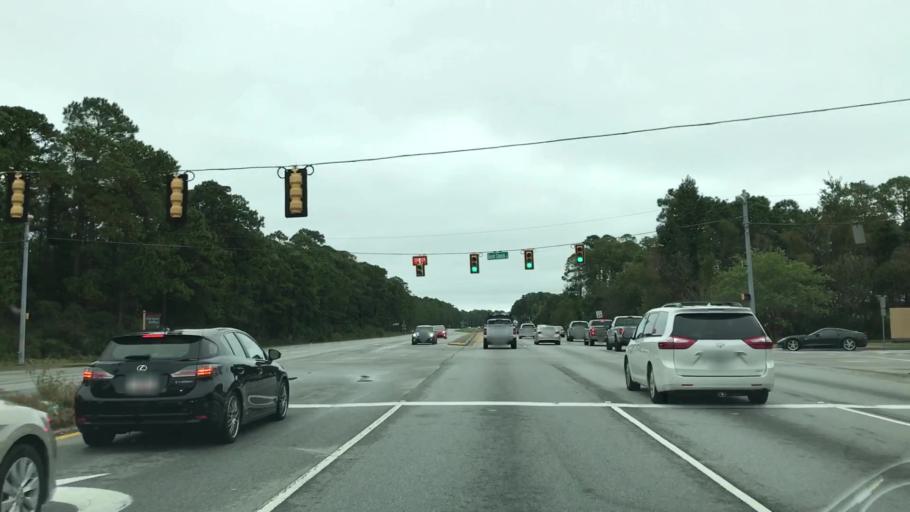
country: US
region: South Carolina
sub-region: Beaufort County
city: Bluffton
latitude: 32.2515
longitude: -80.8429
